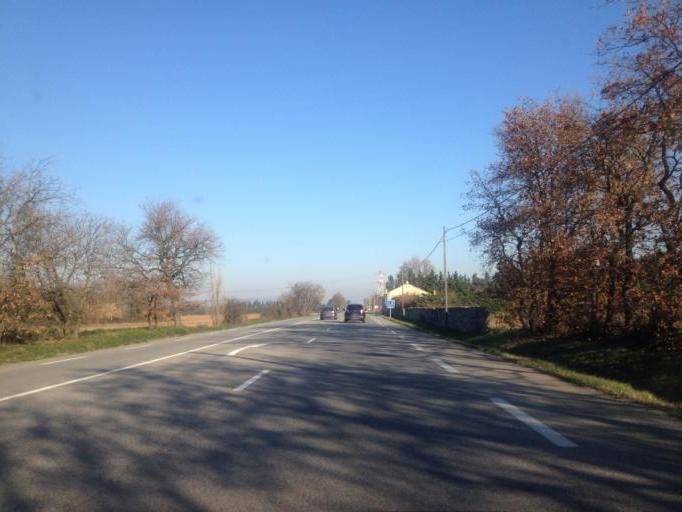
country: FR
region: Provence-Alpes-Cote d'Azur
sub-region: Departement du Vaucluse
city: Lapalud
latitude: 44.3247
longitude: 4.6867
